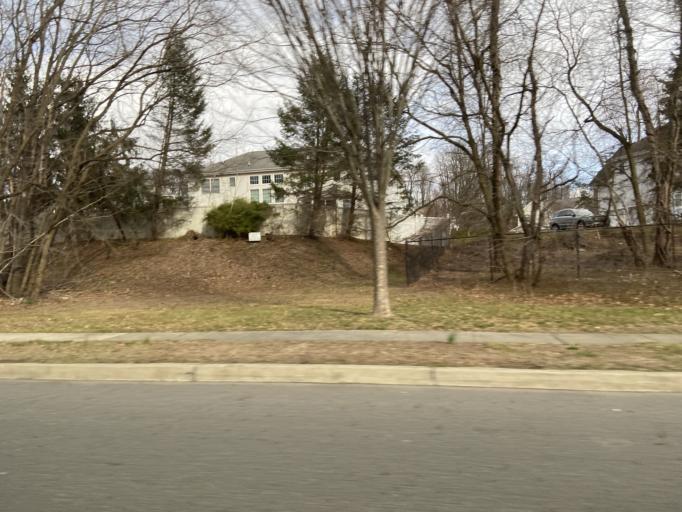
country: US
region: New Jersey
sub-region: Bergen County
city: Paramus
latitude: 40.9290
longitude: -74.0907
